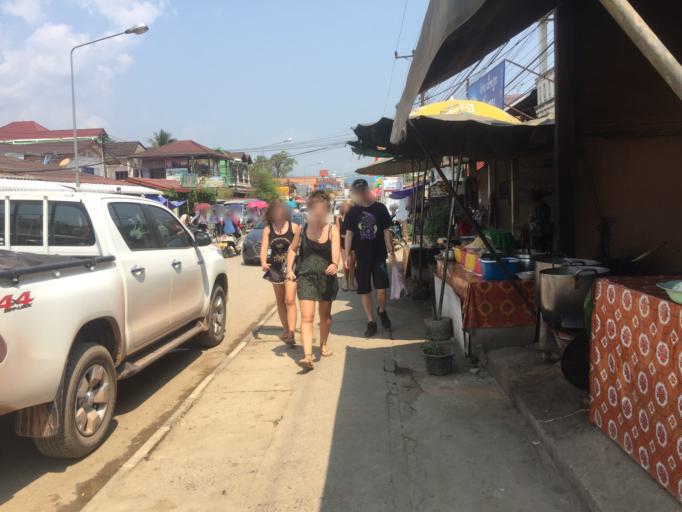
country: LA
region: Vientiane
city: Vangviang
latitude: 18.9245
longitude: 102.4491
